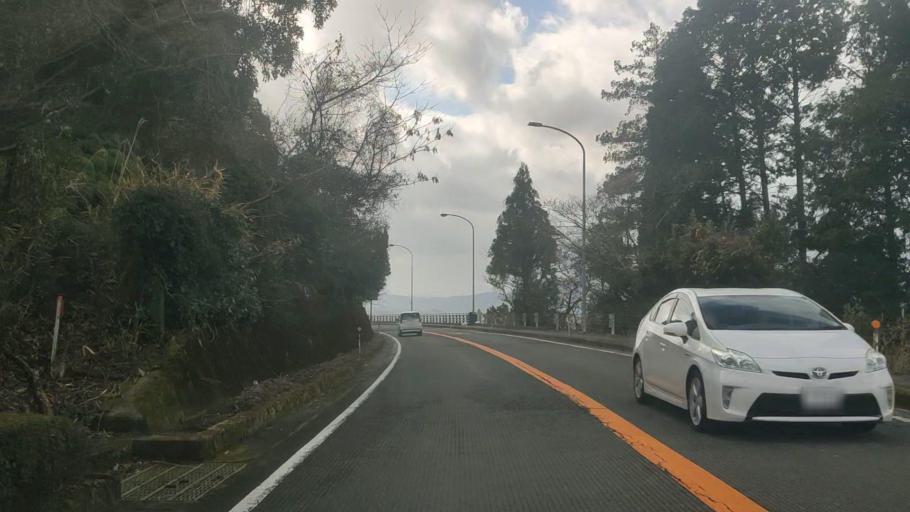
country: JP
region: Kumamoto
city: Hitoyoshi
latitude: 32.0743
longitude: 130.7972
